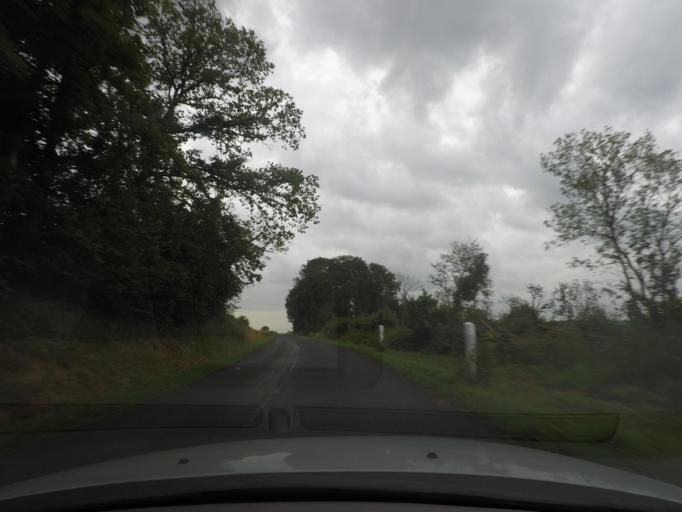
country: FR
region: Haute-Normandie
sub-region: Departement de la Seine-Maritime
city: Neufchatel-en-Bray
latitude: 49.7382
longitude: 1.4826
